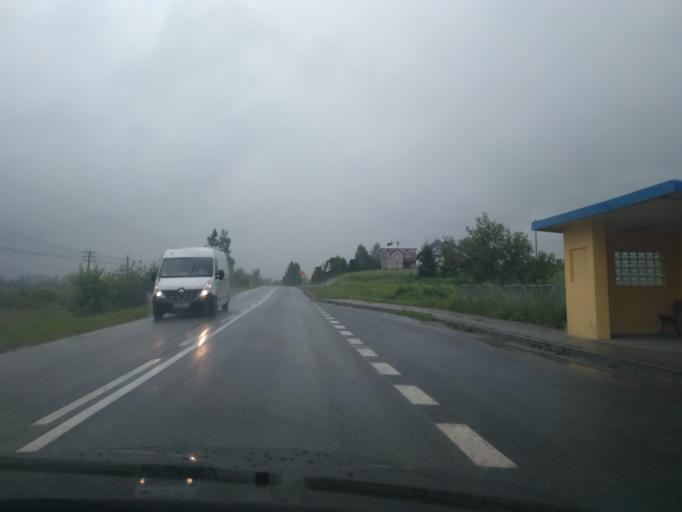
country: PL
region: Subcarpathian Voivodeship
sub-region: Powiat krosnienski
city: Leki
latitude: 49.7981
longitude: 21.6476
